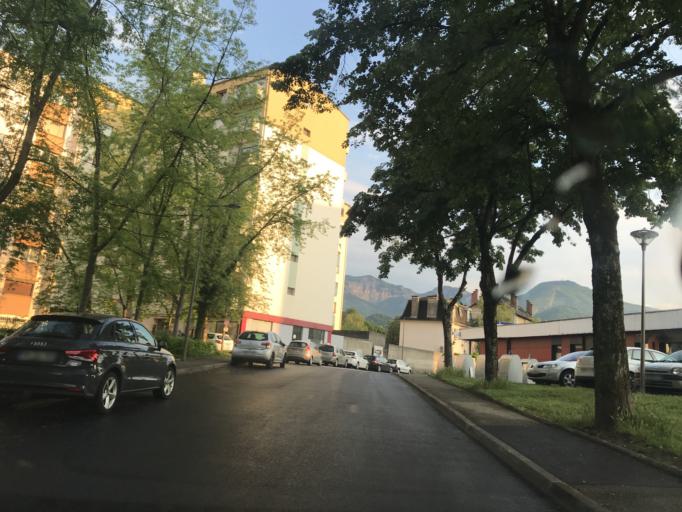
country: FR
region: Rhone-Alpes
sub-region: Departement de la Savoie
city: Cognin
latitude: 45.5615
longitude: 5.8974
